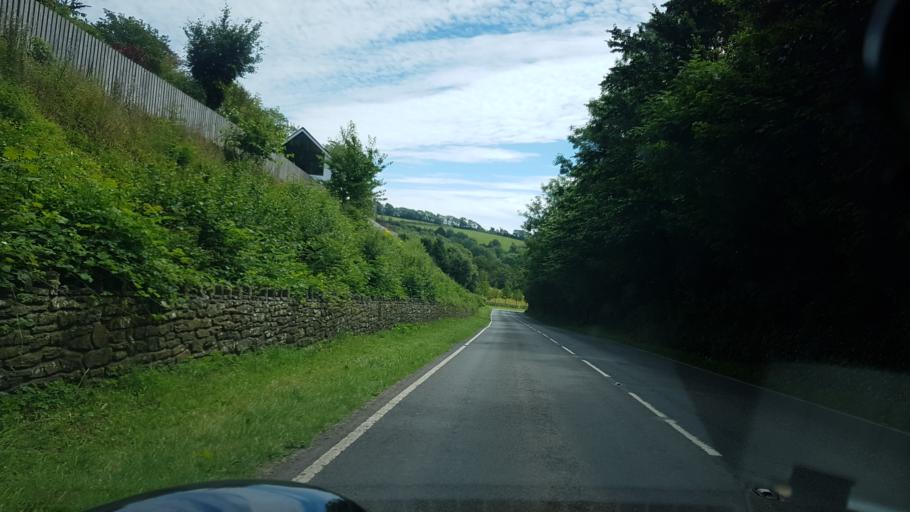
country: GB
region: Wales
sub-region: Carmarthenshire
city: Saint Clears
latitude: 51.7774
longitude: -4.4676
